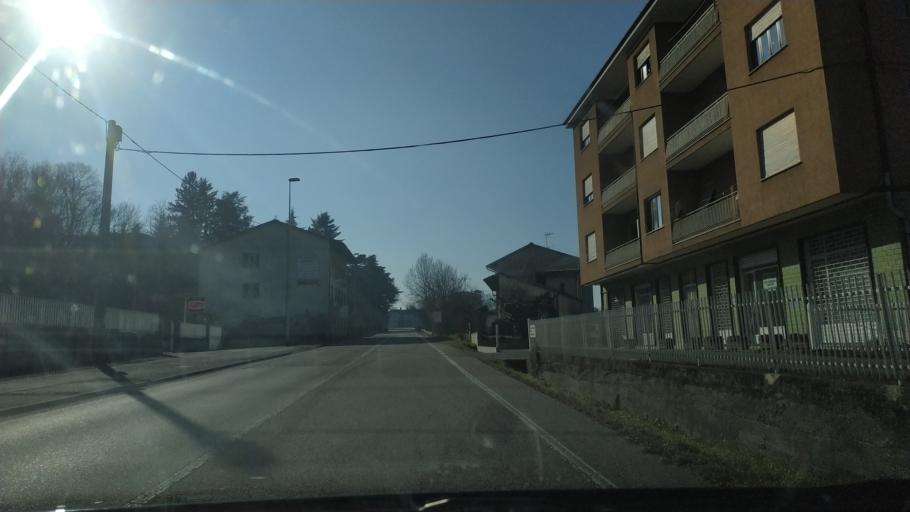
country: IT
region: Piedmont
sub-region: Provincia di Torino
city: Ivrea
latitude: 45.4751
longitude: 7.8665
